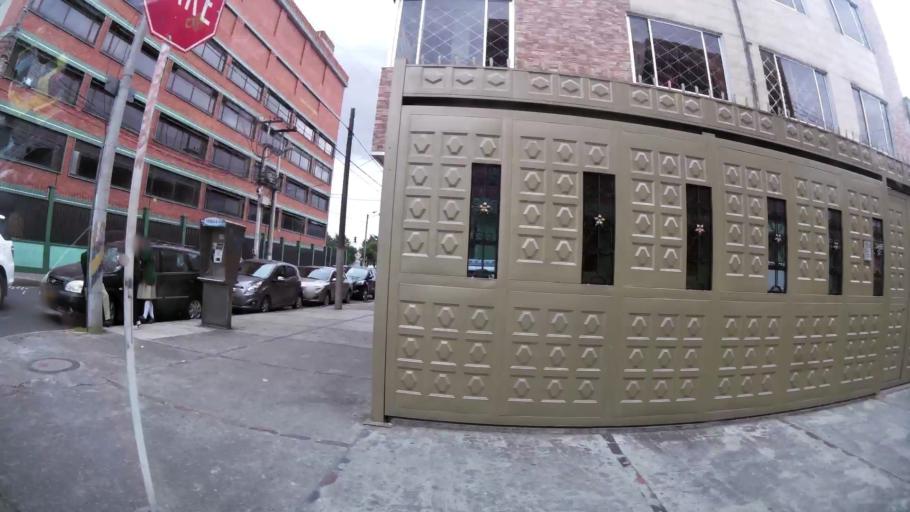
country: CO
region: Bogota D.C.
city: Bogota
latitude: 4.6077
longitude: -74.1008
